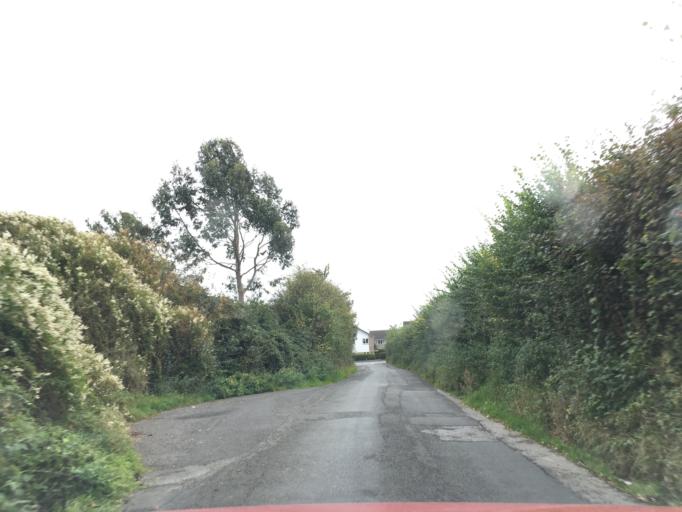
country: GB
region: England
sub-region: Gloucestershire
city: Stonehouse
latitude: 51.7502
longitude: -2.2543
